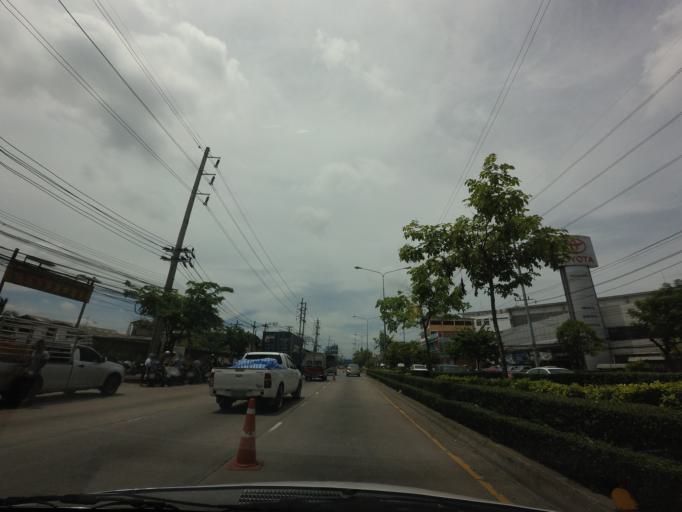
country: TH
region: Samut Prakan
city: Phra Pradaeng
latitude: 13.6429
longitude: 100.5254
